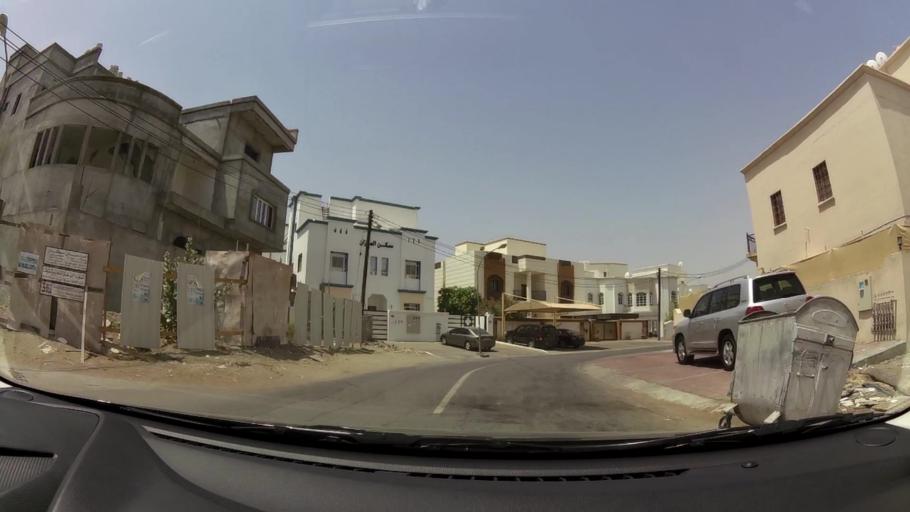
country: OM
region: Muhafazat Masqat
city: Bawshar
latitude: 23.5866
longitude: 58.4418
